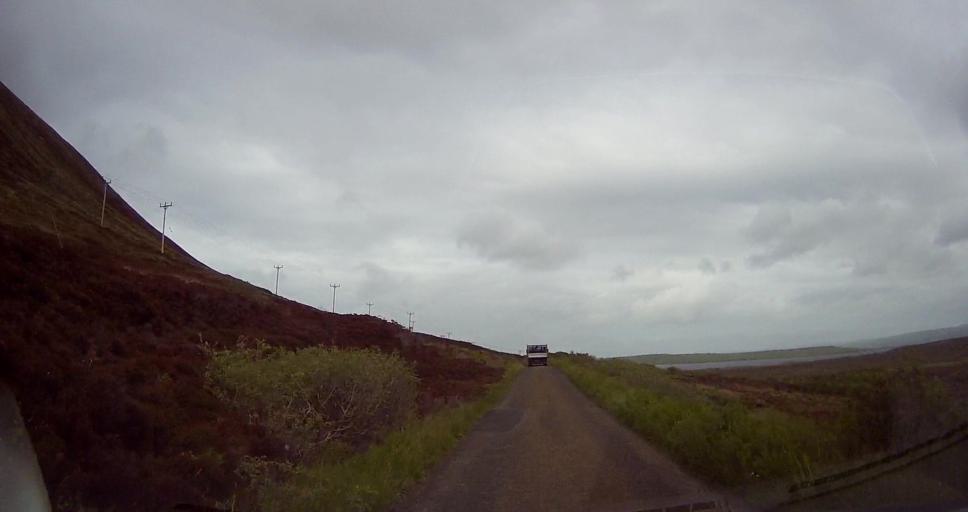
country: GB
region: Scotland
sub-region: Orkney Islands
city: Stromness
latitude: 58.8930
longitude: -3.3145
